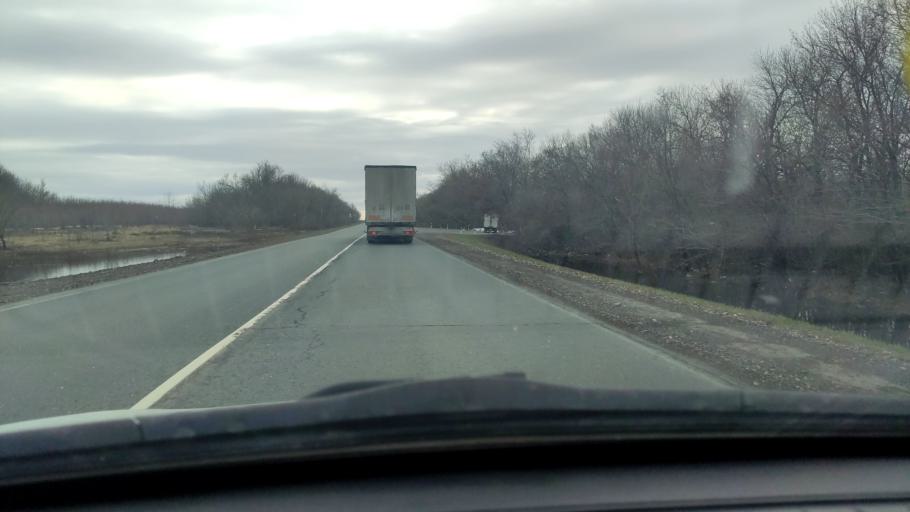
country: RU
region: Samara
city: Zhigulevsk
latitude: 53.3146
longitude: 49.3614
